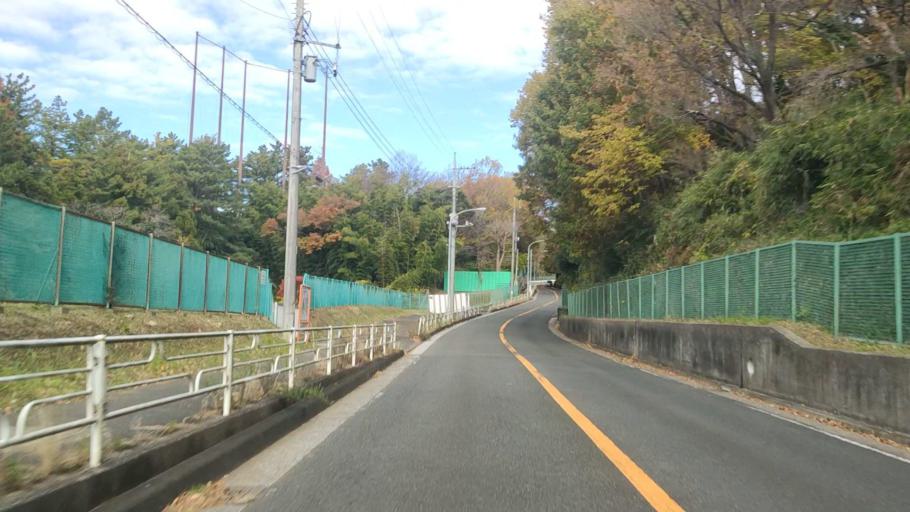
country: JP
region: Kanagawa
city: Yokohama
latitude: 35.4418
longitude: 139.5442
